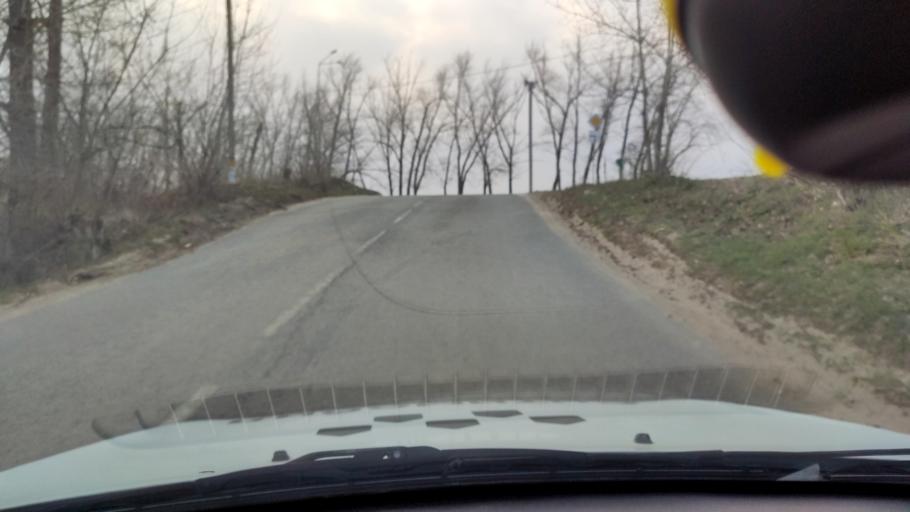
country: RU
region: Samara
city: Zhigulevsk
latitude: 53.4557
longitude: 49.5565
